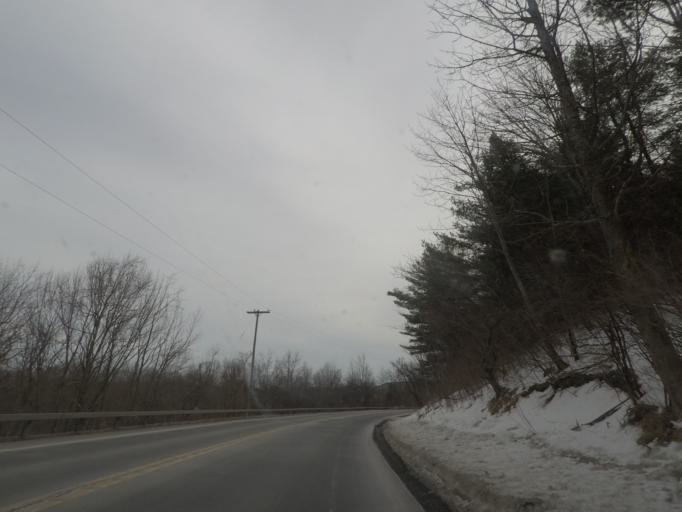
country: US
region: New York
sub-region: Albany County
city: Voorheesville
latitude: 42.5963
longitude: -73.9885
